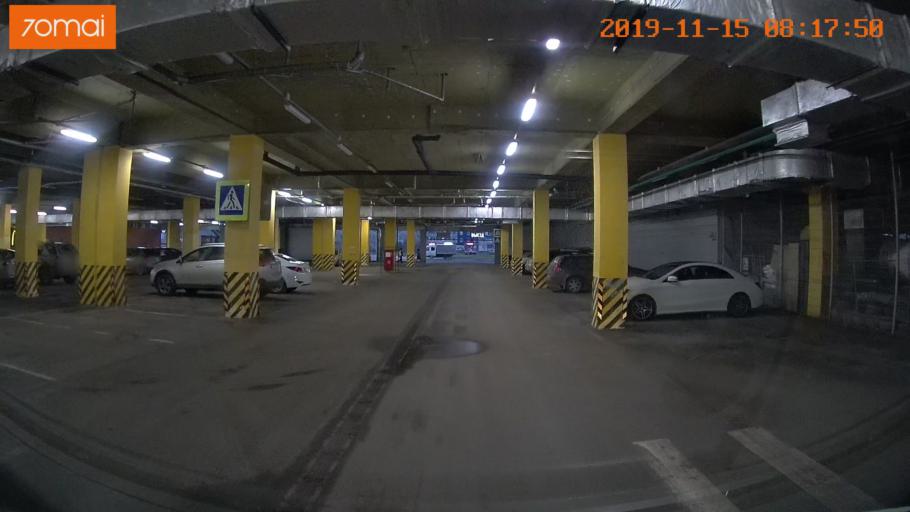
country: RU
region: Vologda
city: Cherepovets
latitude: 59.0921
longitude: 37.9177
